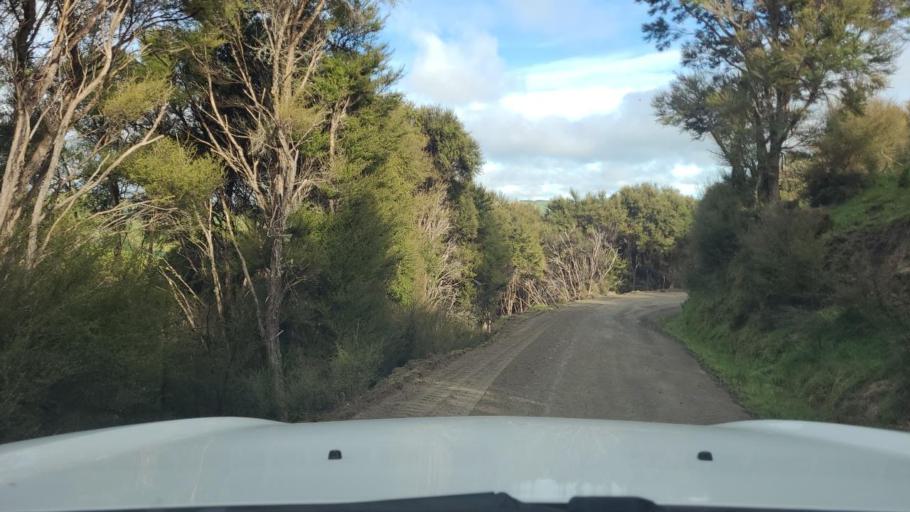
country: NZ
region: Wellington
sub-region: South Wairarapa District
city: Waipawa
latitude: -41.2428
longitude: 175.6967
